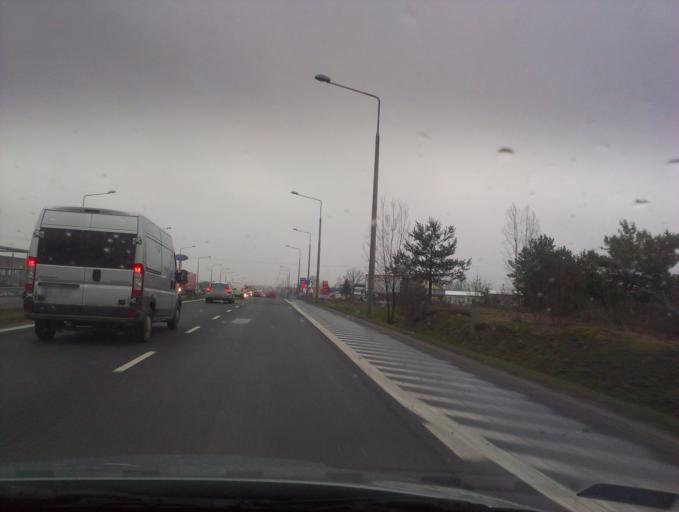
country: PL
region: Masovian Voivodeship
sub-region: Radom
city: Radom
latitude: 51.4577
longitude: 21.1408
